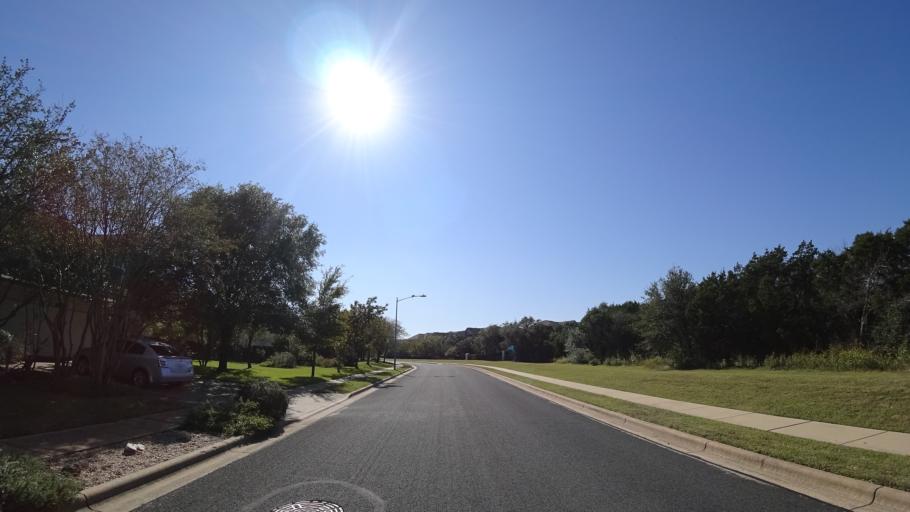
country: US
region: Texas
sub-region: Travis County
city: Shady Hollow
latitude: 30.2020
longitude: -97.8602
